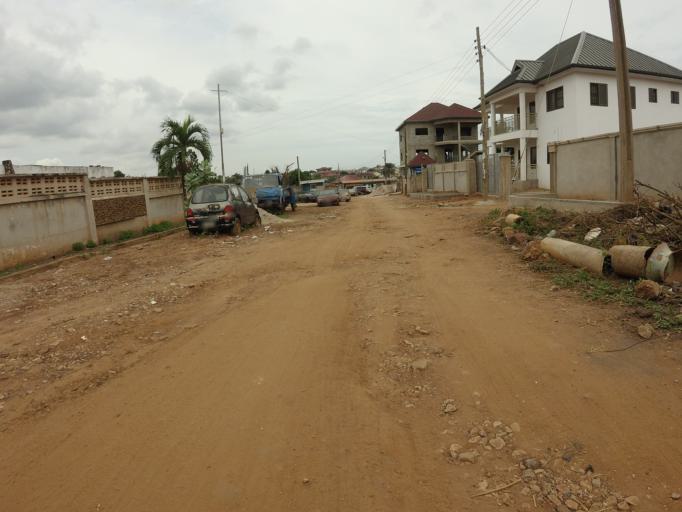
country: GH
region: Greater Accra
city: Dome
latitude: 5.6050
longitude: -0.2234
